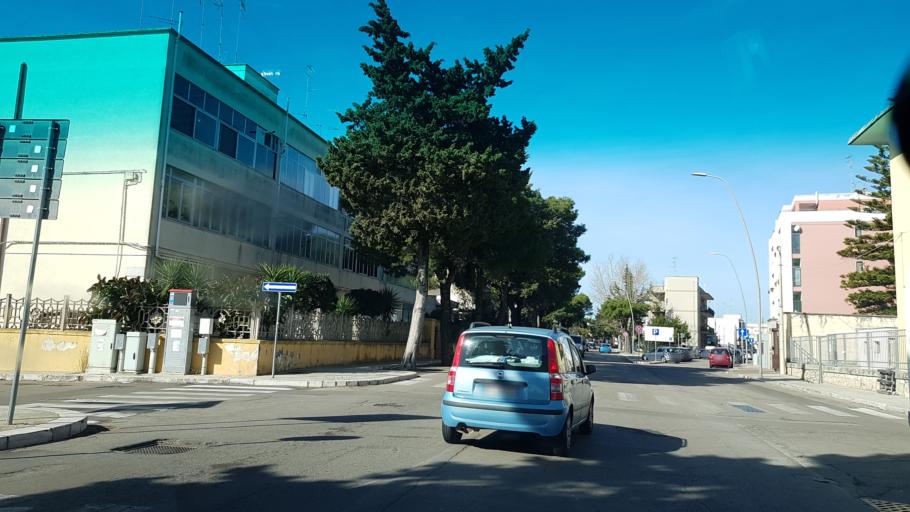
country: IT
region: Apulia
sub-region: Provincia di Lecce
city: Lecce
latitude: 40.3444
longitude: 18.1573
